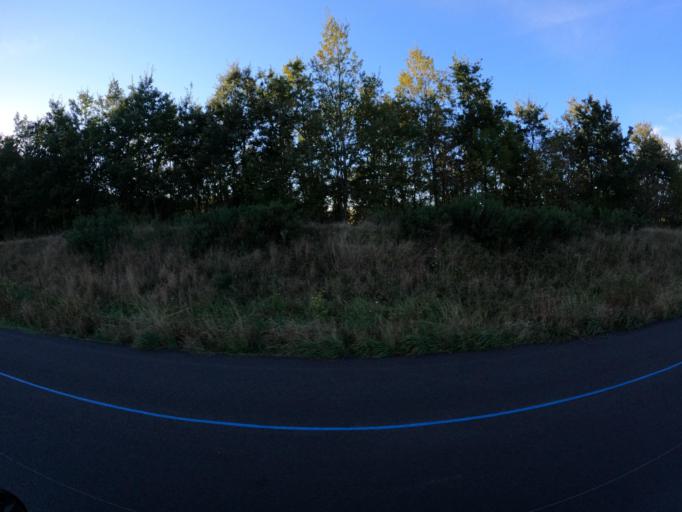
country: FR
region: Pays de la Loire
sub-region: Departement de la Vendee
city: Mortagne-sur-Sevre
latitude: 46.9537
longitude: -0.9413
